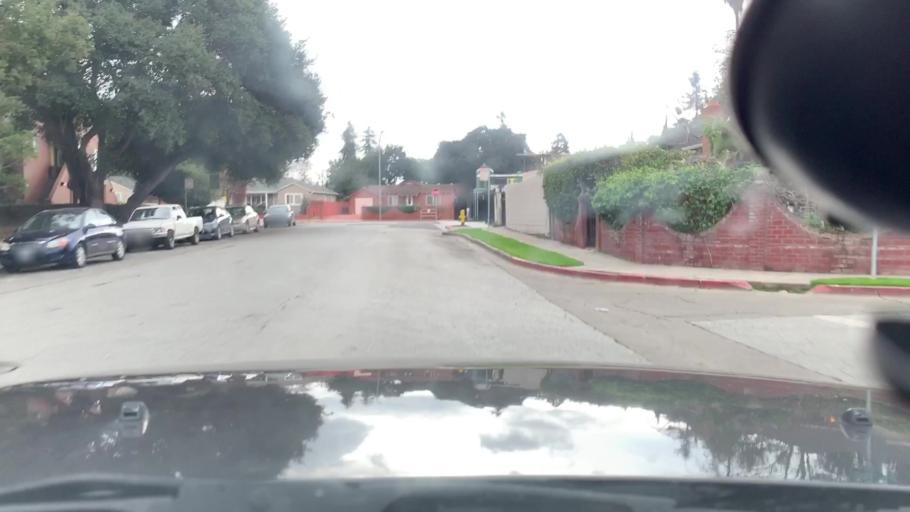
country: US
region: California
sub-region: San Mateo County
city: East Palo Alto
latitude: 37.4721
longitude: -122.1420
